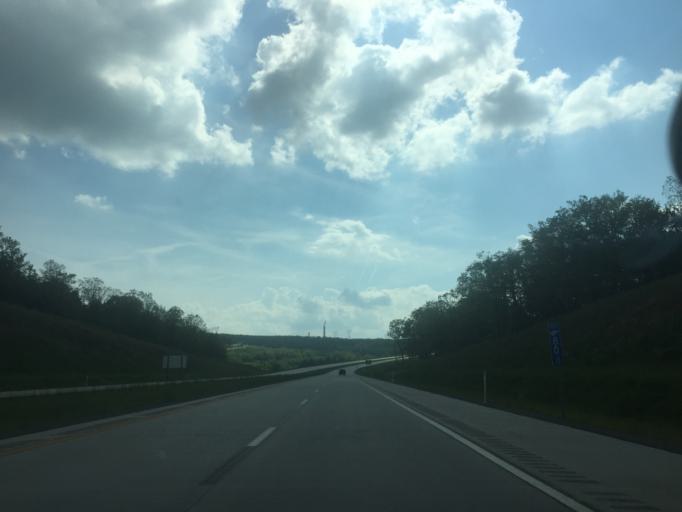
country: US
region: Maryland
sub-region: Garrett County
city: Mountain Lake Park
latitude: 39.2163
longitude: -79.2227
